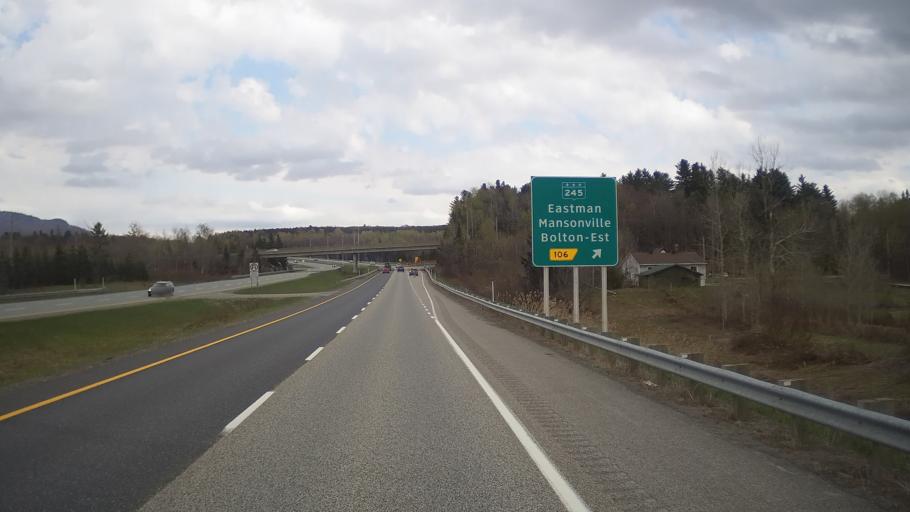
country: CA
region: Quebec
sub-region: Estrie
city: Magog
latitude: 45.2988
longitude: -72.3214
